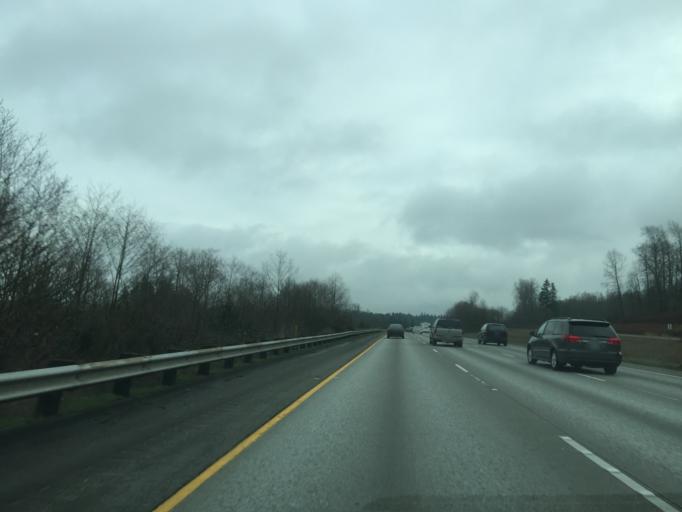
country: US
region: Washington
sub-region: Snohomish County
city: Bryant
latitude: 48.2263
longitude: -122.2276
